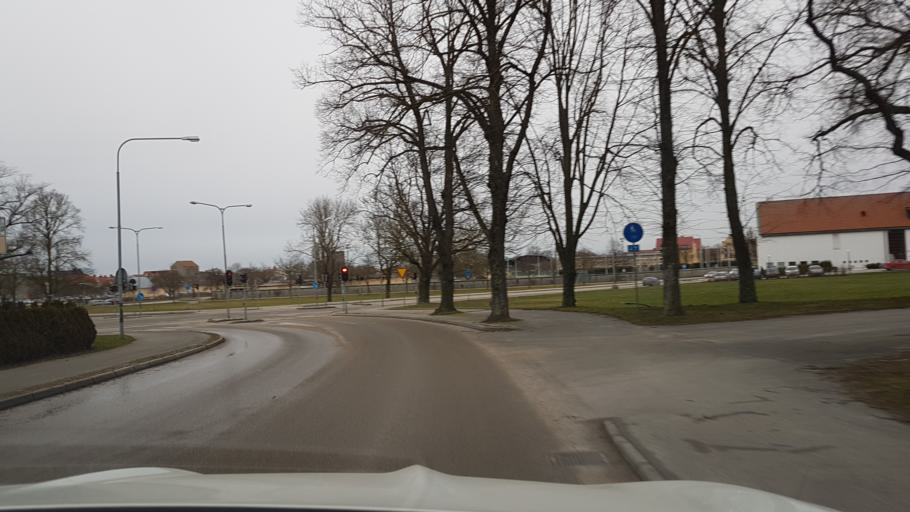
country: SE
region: Gotland
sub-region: Gotland
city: Visby
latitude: 57.6327
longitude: 18.2952
